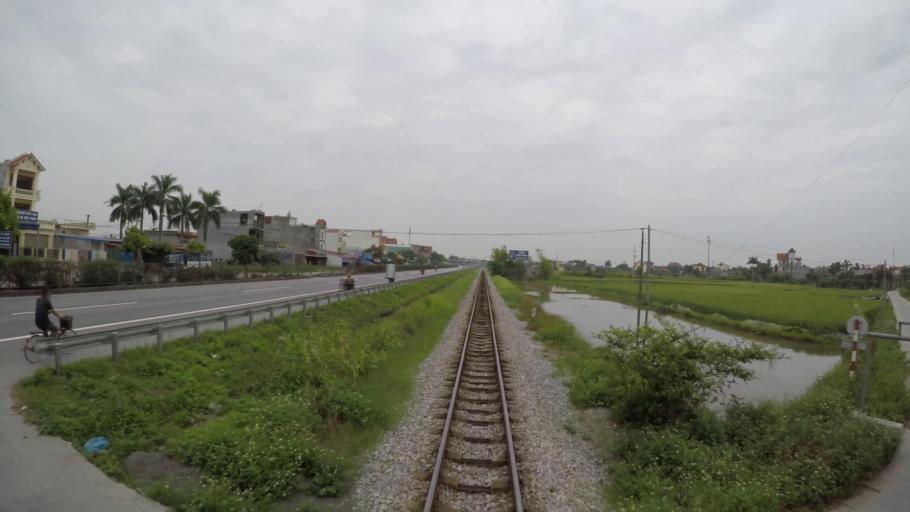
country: VN
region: Hai Duong
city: Phu Thai
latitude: 20.9292
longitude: 106.5548
